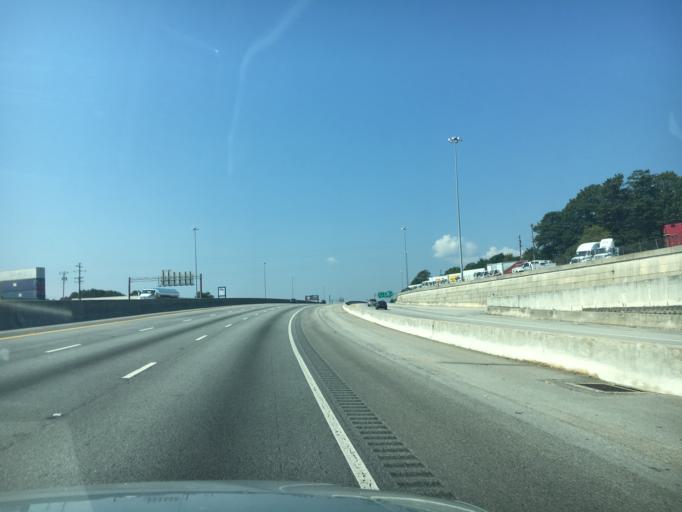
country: US
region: South Carolina
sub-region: Greenville County
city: Gantt
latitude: 34.7912
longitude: -82.4175
